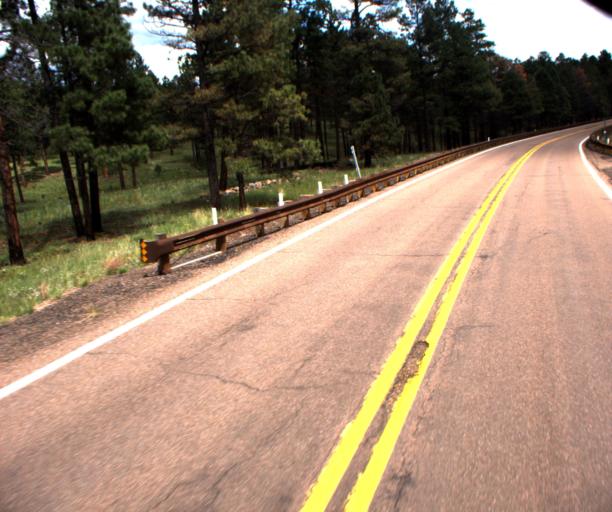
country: US
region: Arizona
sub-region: Apache County
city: Eagar
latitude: 34.0772
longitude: -109.4736
